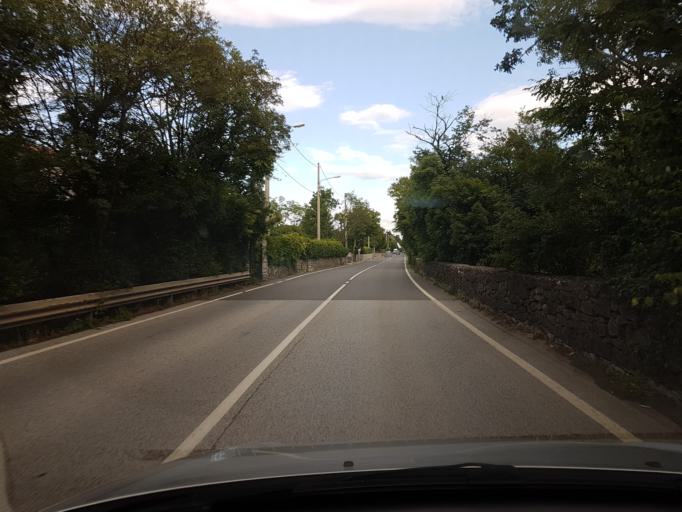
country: IT
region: Friuli Venezia Giulia
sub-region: Provincia di Trieste
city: Villa Opicina
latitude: 45.6839
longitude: 13.7990
